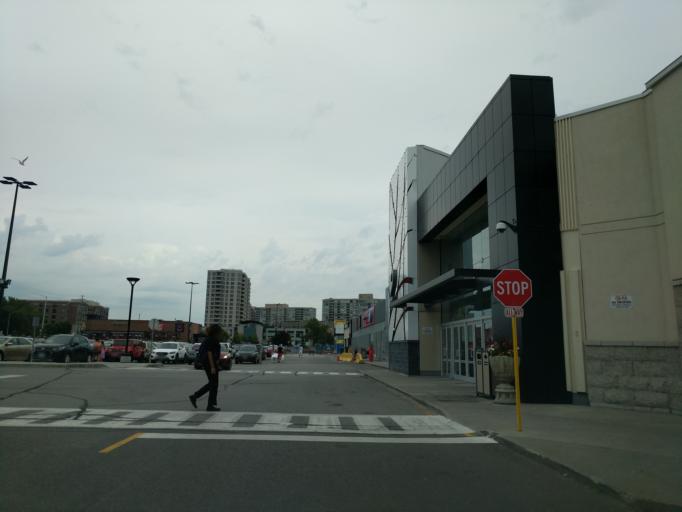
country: CA
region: Ontario
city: Ajax
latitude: 43.8365
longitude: -79.0877
